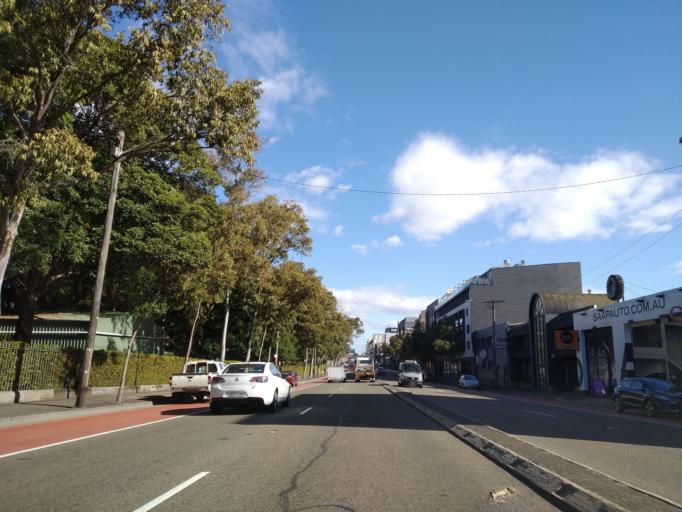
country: AU
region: New South Wales
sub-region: Marrickville
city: Camperdown
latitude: -33.8854
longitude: 151.1829
